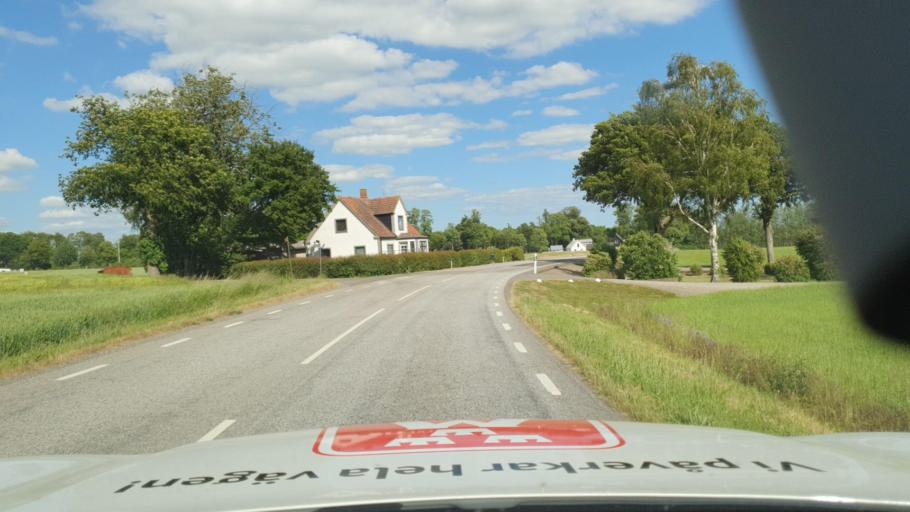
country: SE
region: Skane
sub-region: Ystads Kommun
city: Kopingebro
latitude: 55.4769
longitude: 13.8913
